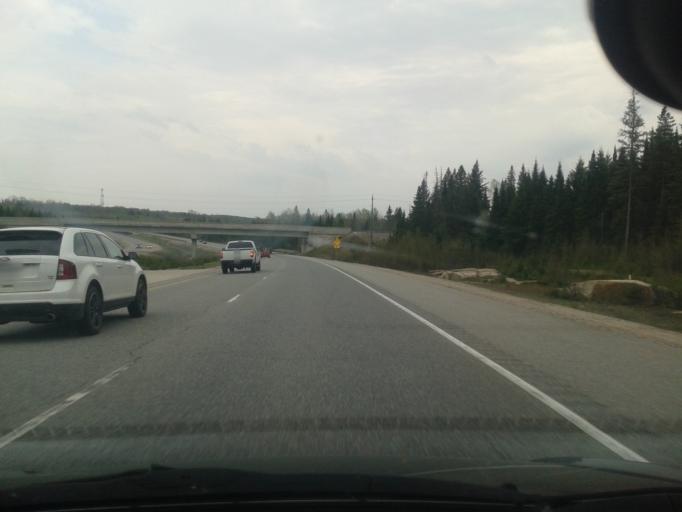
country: CA
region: Ontario
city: Powassan
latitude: 45.9843
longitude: -79.3833
